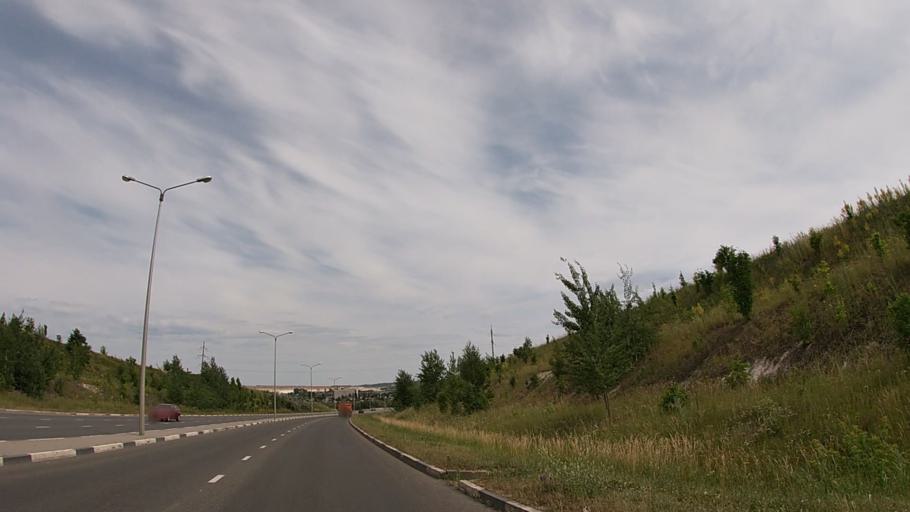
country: RU
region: Belgorod
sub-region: Belgorodskiy Rayon
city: Belgorod
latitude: 50.6034
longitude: 36.5299
